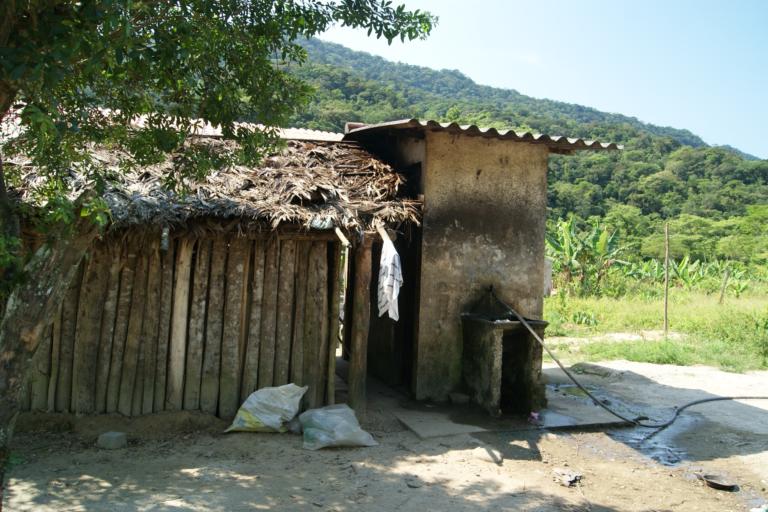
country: BR
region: Sao Paulo
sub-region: Mongagua
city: Mongagua
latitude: -24.0193
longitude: -46.6933
